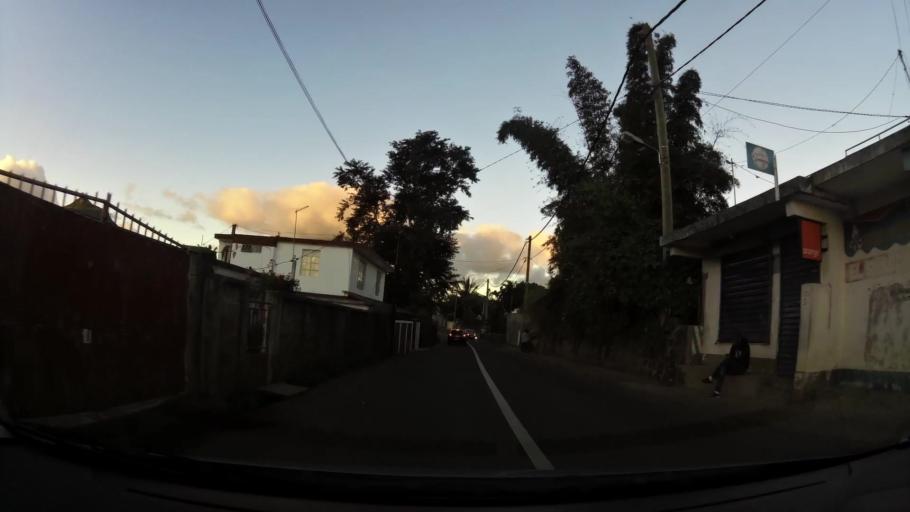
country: MU
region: Moka
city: Saint Pierre
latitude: -20.2194
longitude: 57.5165
